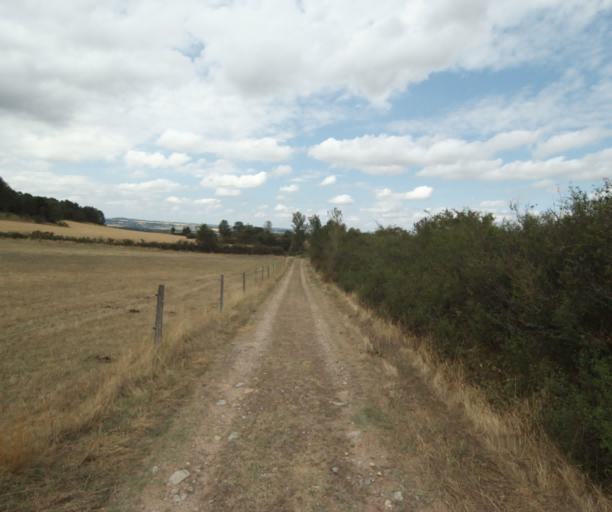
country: FR
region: Midi-Pyrenees
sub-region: Departement de la Haute-Garonne
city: Revel
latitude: 43.4406
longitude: 1.9958
